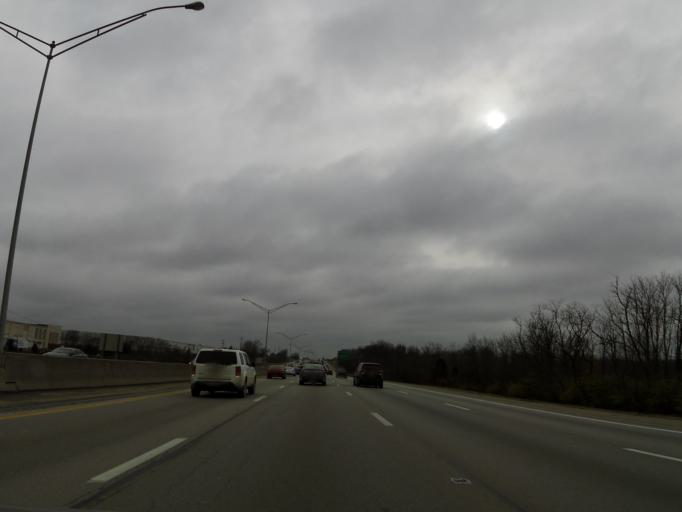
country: US
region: Kentucky
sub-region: Boone County
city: Walton
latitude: 38.9048
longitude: -84.6278
